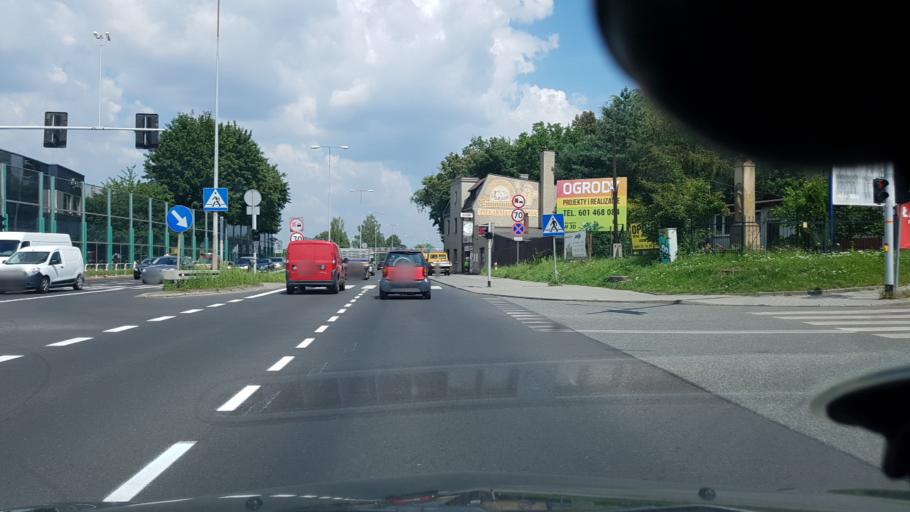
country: PL
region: Silesian Voivodeship
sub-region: Powiat mikolowski
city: Mikolow
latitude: 50.1878
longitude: 18.9193
